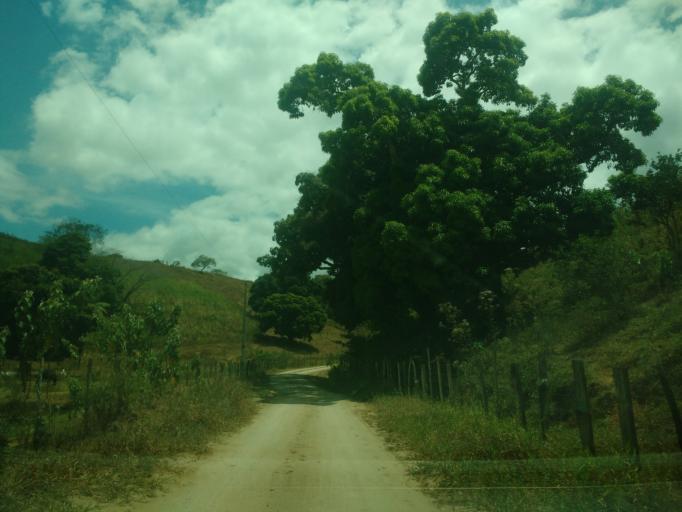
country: BR
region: Alagoas
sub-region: Santana Do Mundau
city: Santana do Mundau
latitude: -9.1525
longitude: -36.1687
